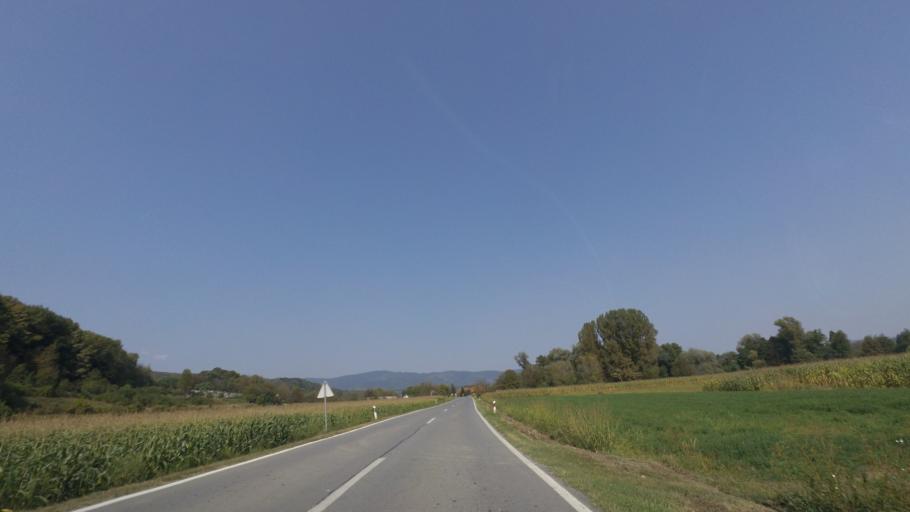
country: HR
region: Brodsko-Posavska
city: Resetari
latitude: 45.3614
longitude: 17.5402
